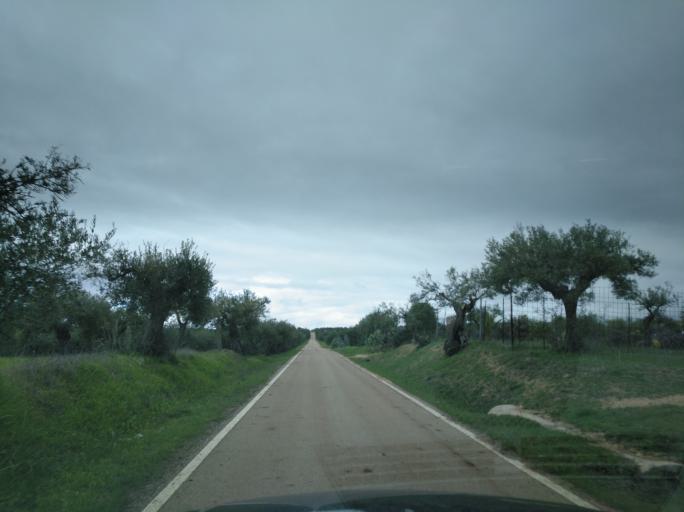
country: PT
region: Portalegre
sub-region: Campo Maior
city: Campo Maior
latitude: 38.9835
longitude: -7.0361
